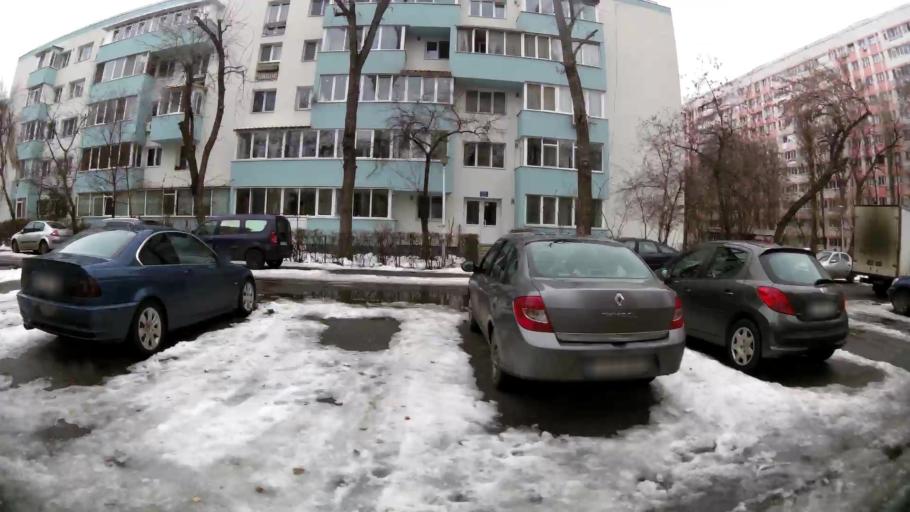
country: RO
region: Ilfov
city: Dobroesti
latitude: 44.4254
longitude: 26.1760
